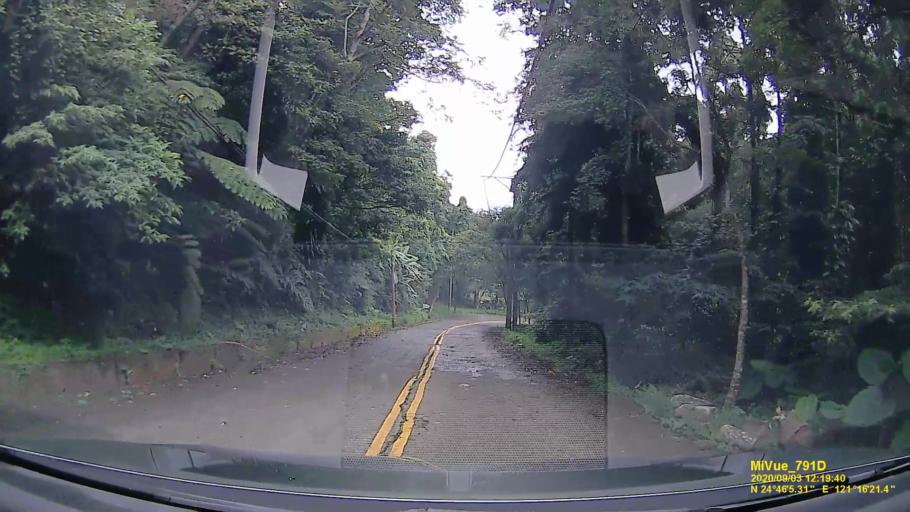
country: TW
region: Taiwan
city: Daxi
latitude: 24.7682
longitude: 121.2725
